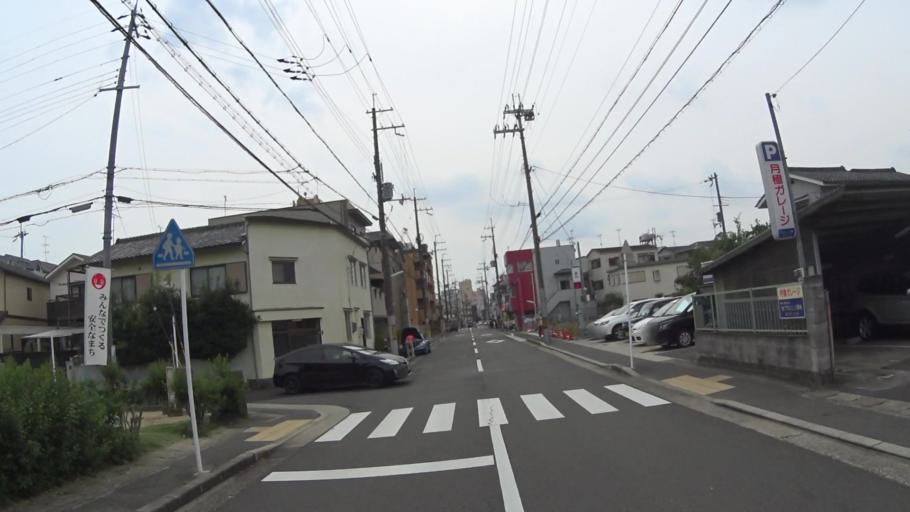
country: JP
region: Kyoto
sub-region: Kyoto-shi
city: Kamigyo-ku
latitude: 35.0480
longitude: 135.7879
